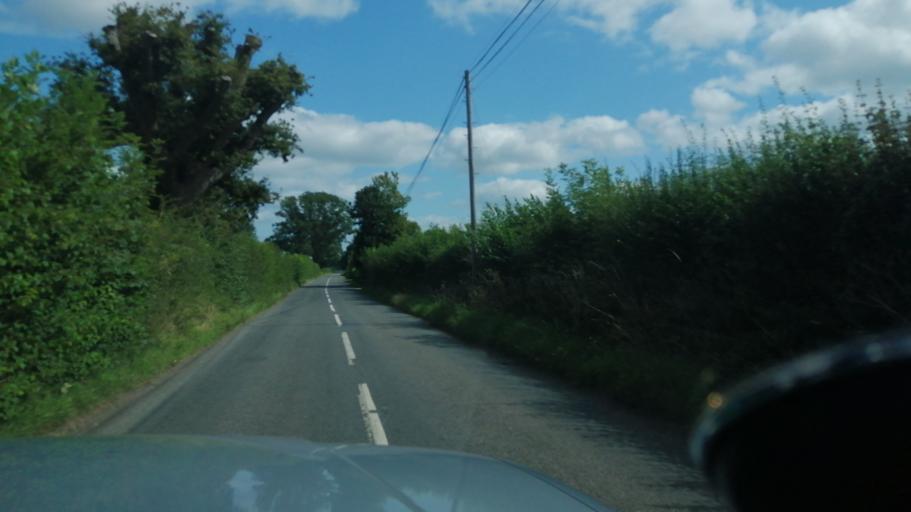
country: GB
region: England
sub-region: Herefordshire
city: Moccas
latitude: 52.0775
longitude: -2.9460
